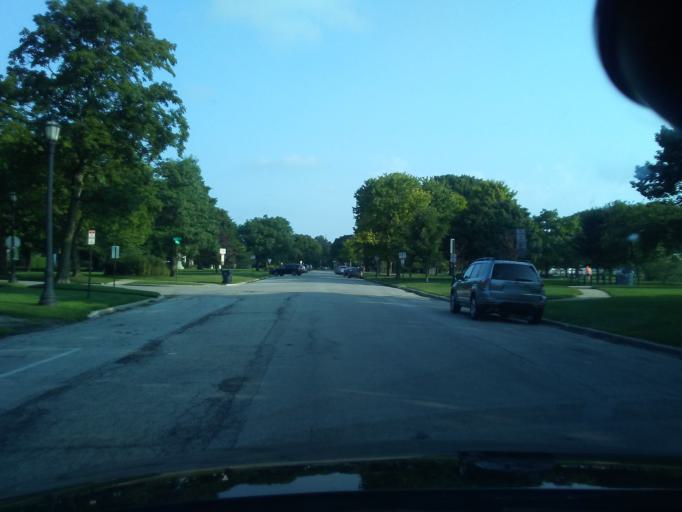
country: US
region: Illinois
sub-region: Cook County
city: Evanston
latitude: 42.0443
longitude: -87.6732
